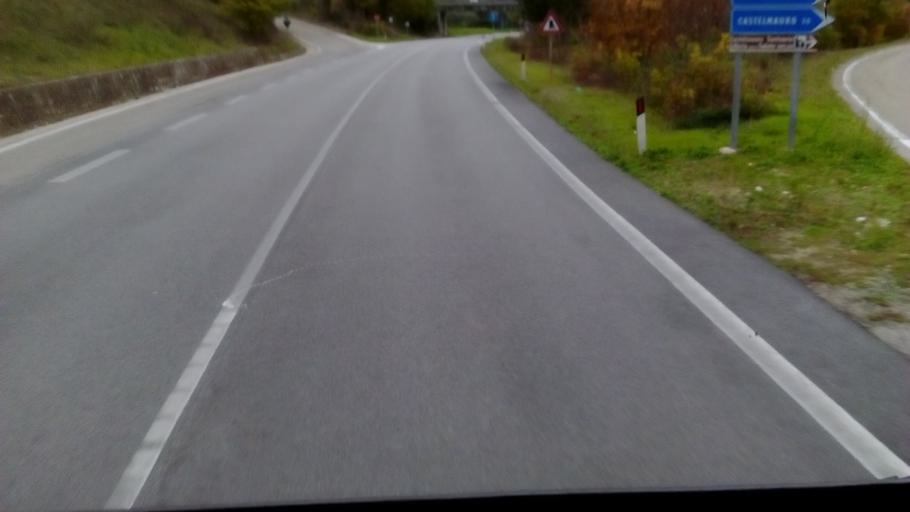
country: IT
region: Molise
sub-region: Provincia di Campobasso
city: Roccavivara
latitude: 41.8566
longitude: 14.6045
